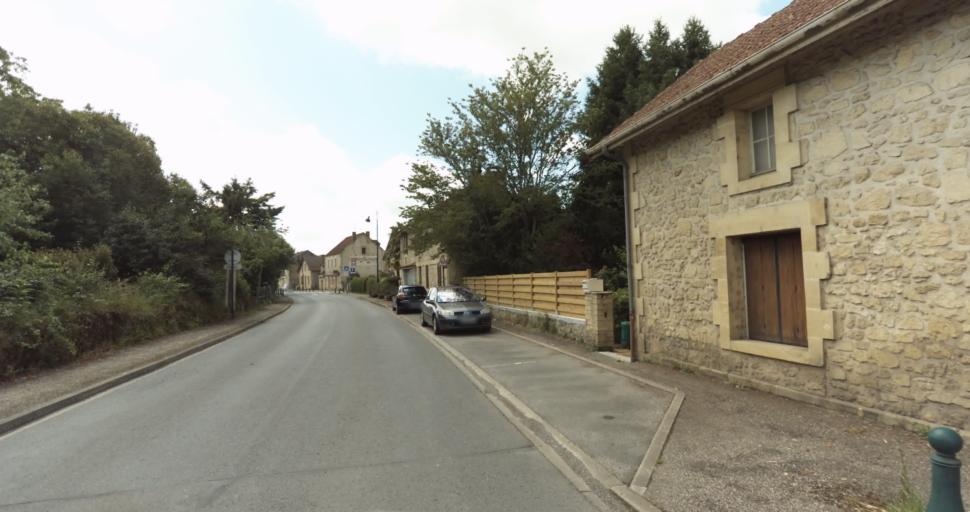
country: FR
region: Aquitaine
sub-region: Departement de la Dordogne
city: Lalinde
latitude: 44.8300
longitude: 0.7038
